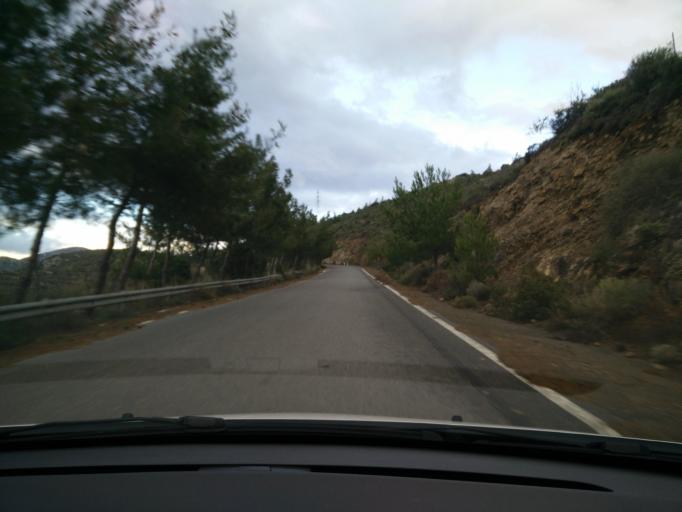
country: GR
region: Crete
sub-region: Nomos Lasithiou
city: Gra Liyia
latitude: 35.0893
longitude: 25.6987
